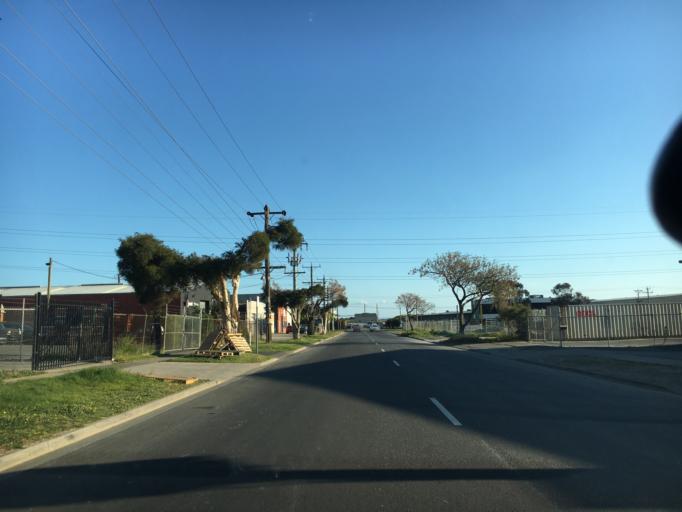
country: AU
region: Victoria
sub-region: Kingston
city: Clayton South
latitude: -37.9401
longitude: 145.1265
